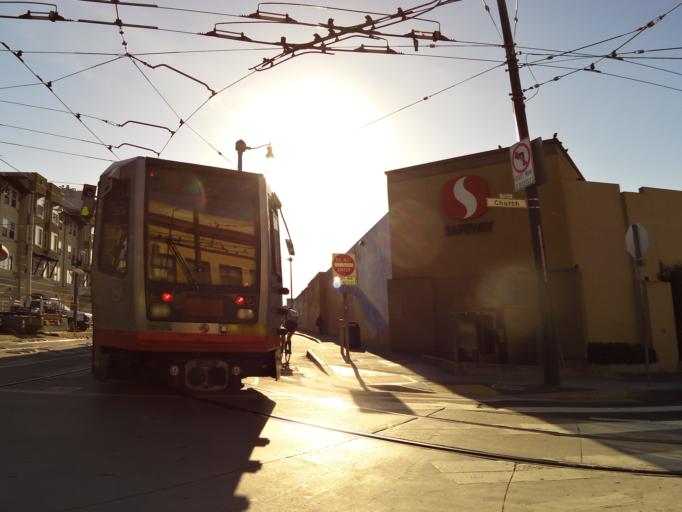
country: US
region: California
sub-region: San Francisco County
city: San Francisco
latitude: 37.7694
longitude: -122.4292
